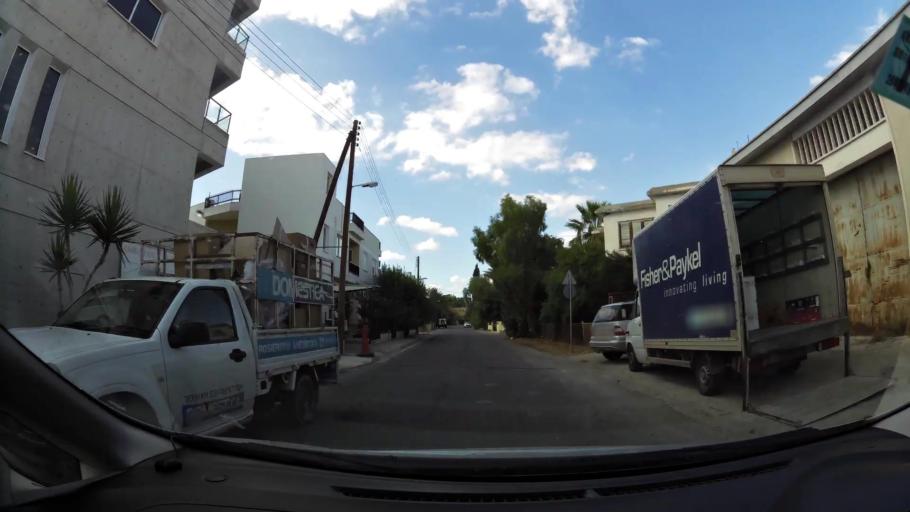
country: CY
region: Lefkosia
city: Nicosia
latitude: 35.1834
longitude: 33.3745
